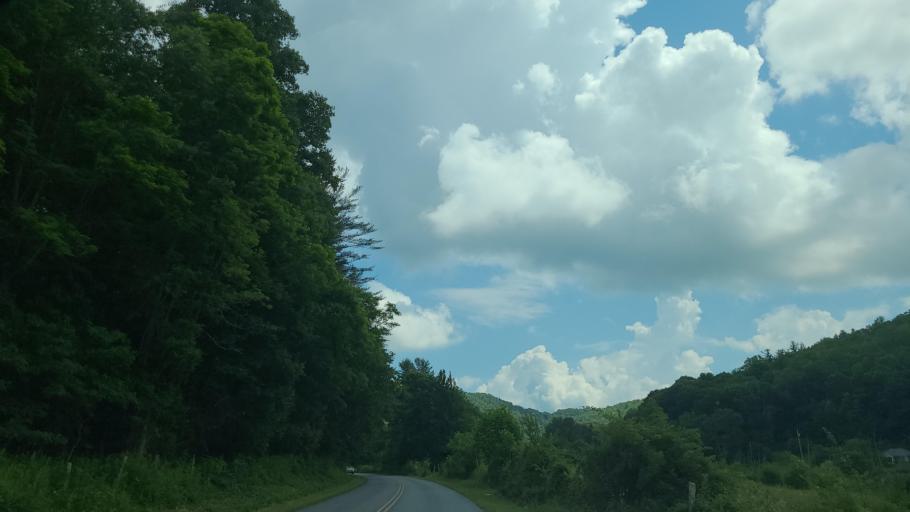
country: US
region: North Carolina
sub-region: Avery County
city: Newland
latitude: 35.9821
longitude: -81.9124
